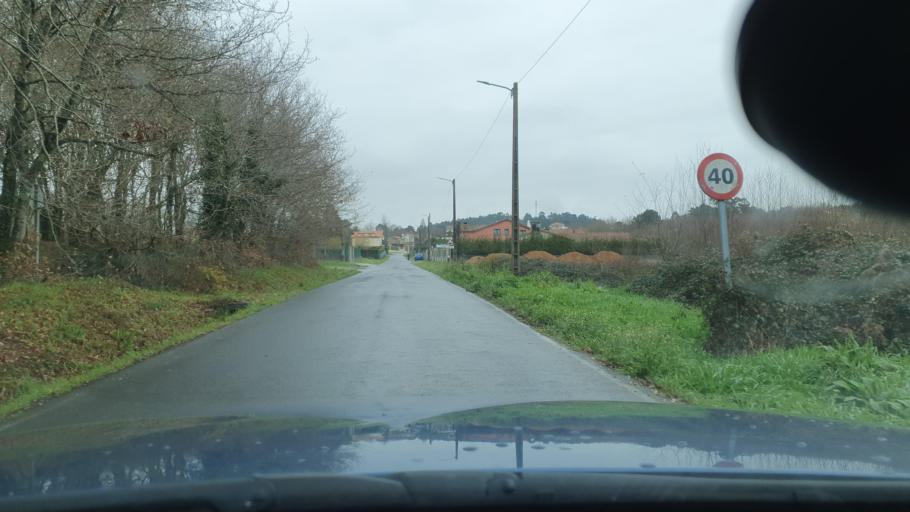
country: ES
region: Galicia
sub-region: Provincia da Coruna
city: Ames
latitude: 42.8305
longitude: -8.6082
